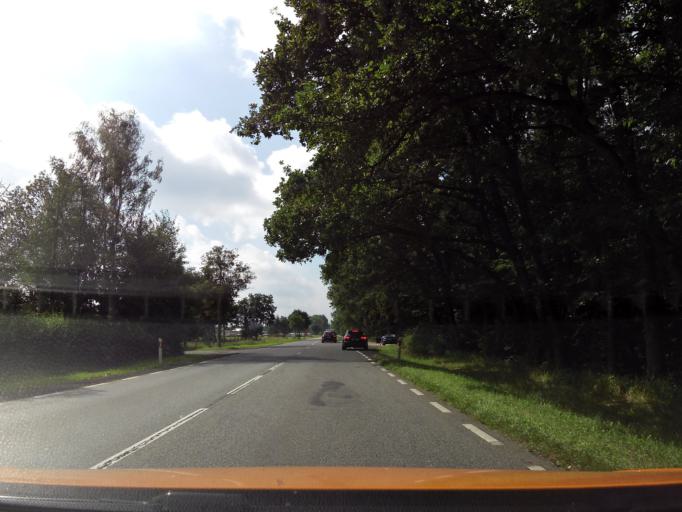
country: PL
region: West Pomeranian Voivodeship
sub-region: Powiat gryficki
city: Ploty
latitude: 53.8199
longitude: 15.2821
